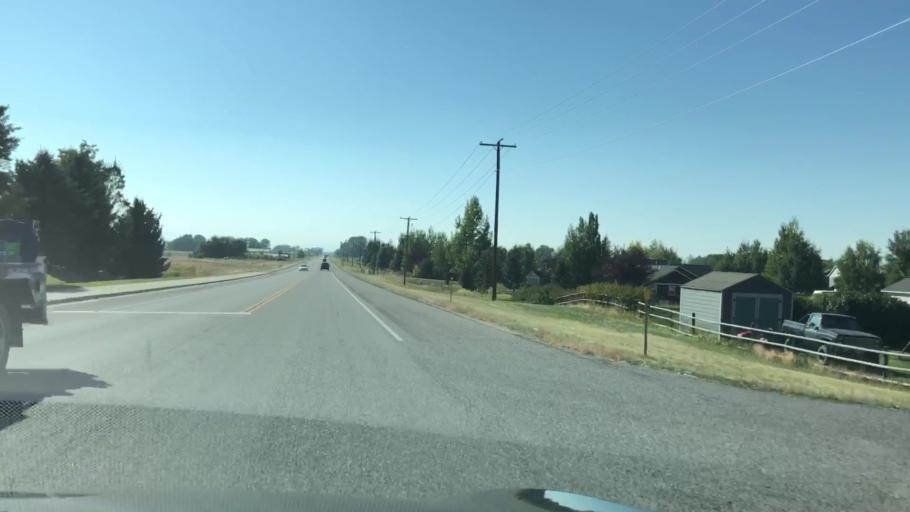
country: US
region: Montana
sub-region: Gallatin County
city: Belgrade
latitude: 45.7293
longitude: -111.1398
